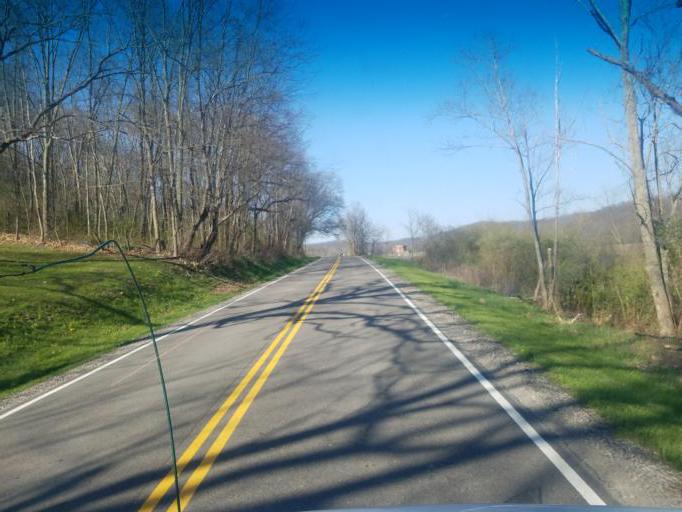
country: US
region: Ohio
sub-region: Knox County
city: Oak Hill
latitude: 40.3231
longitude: -82.0784
